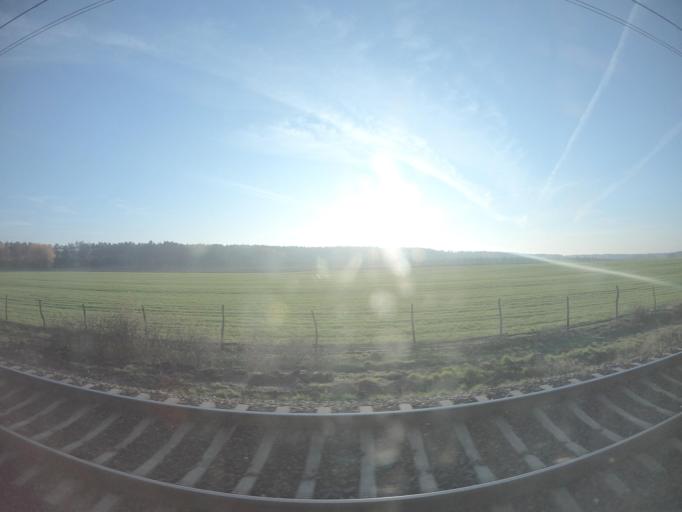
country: PL
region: Lubusz
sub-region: Powiat slubicki
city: Rzepin
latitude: 52.2776
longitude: 14.9098
